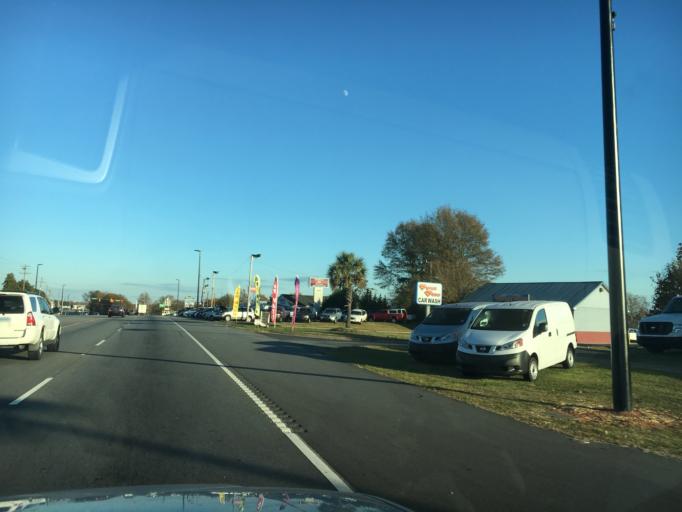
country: US
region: South Carolina
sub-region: Greenville County
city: Greer
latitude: 34.9473
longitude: -82.2101
